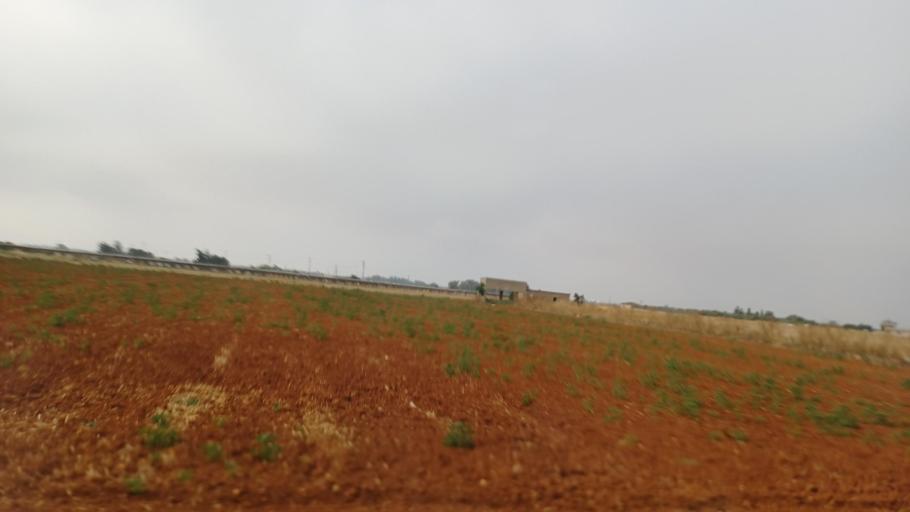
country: CY
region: Ammochostos
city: Achna
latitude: 35.0562
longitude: 33.7992
